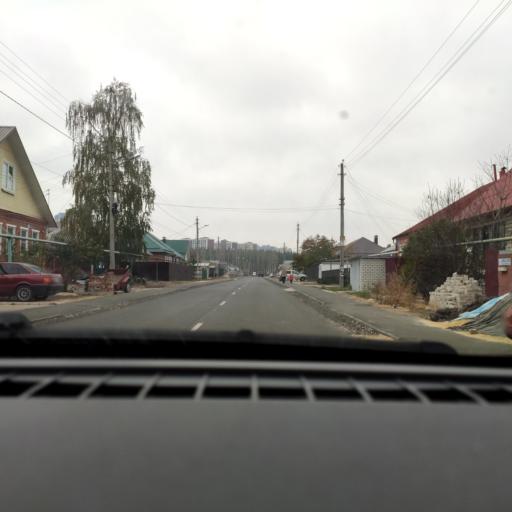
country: RU
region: Voronezj
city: Somovo
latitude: 51.7459
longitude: 39.3262
